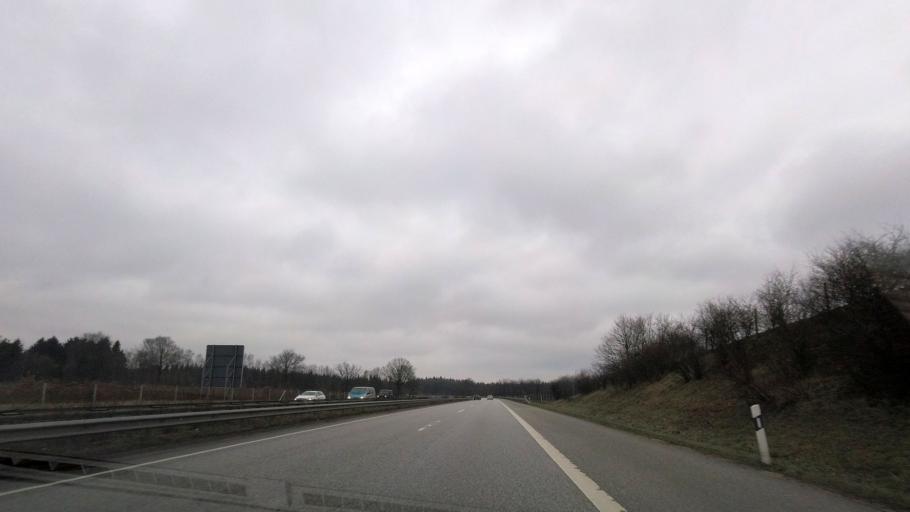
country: DE
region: Schleswig-Holstein
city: Daldorf
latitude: 54.0224
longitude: 10.2442
